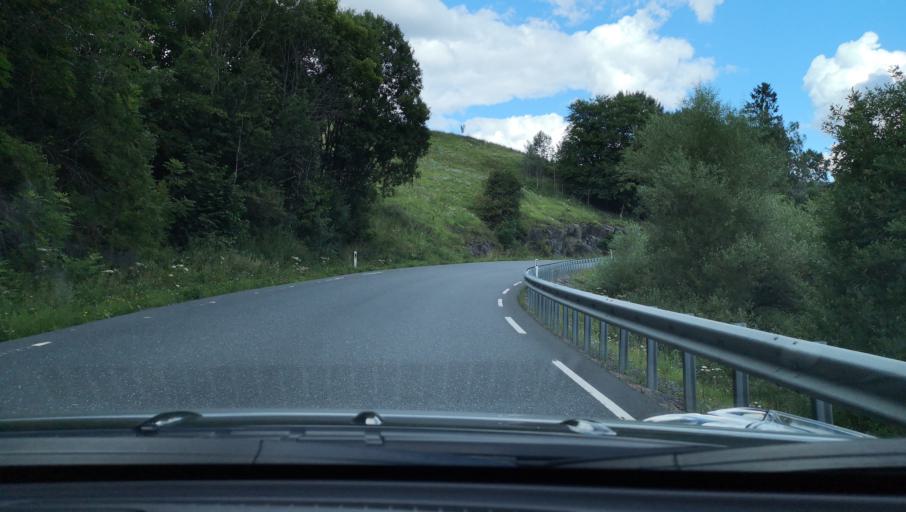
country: NO
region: Ostfold
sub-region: Hobol
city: Tomter
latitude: 59.6439
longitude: 10.9810
